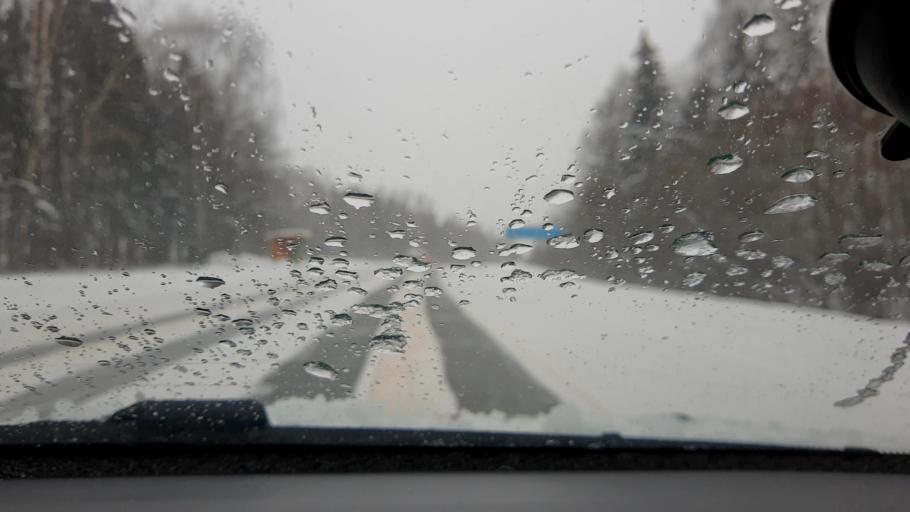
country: RU
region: Nizjnij Novgorod
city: Pervomayskiy
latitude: 56.6281
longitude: 43.2419
